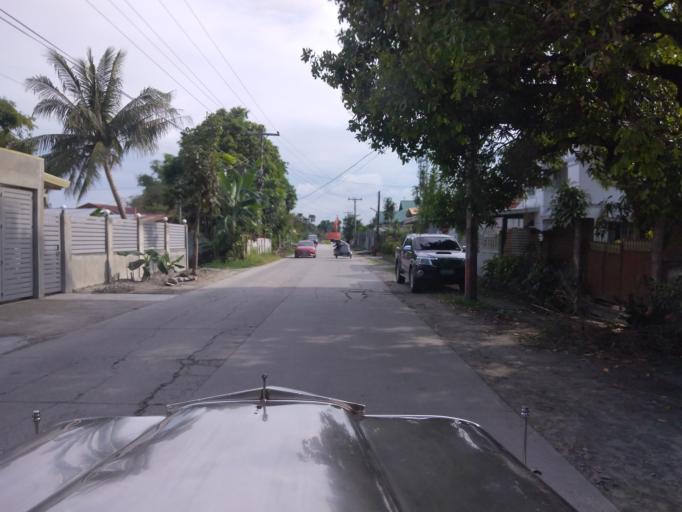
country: PH
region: Central Luzon
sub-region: Province of Pampanga
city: San Patricio
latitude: 15.0961
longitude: 120.7109
